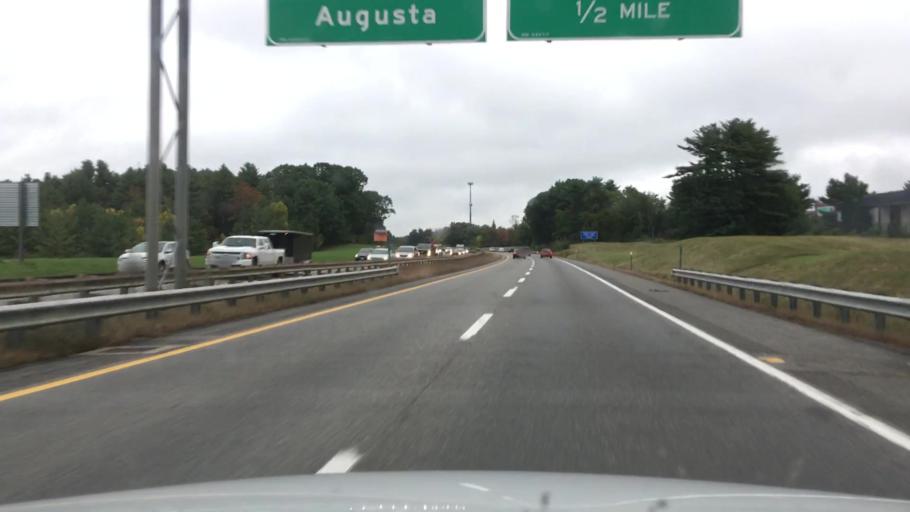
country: US
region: Maine
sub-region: Cumberland County
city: Falmouth
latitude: 43.7107
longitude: -70.3085
